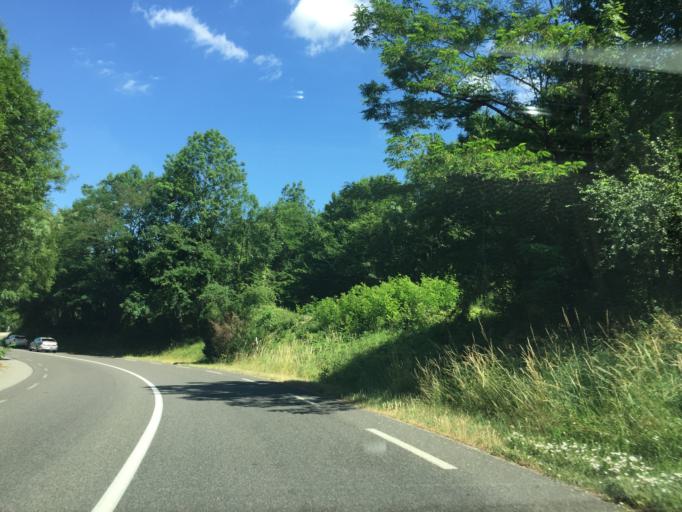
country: FR
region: Rhone-Alpes
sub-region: Departement de l'Isere
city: Saint-Hilaire-du-Rosier
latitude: 45.0656
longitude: 5.2364
